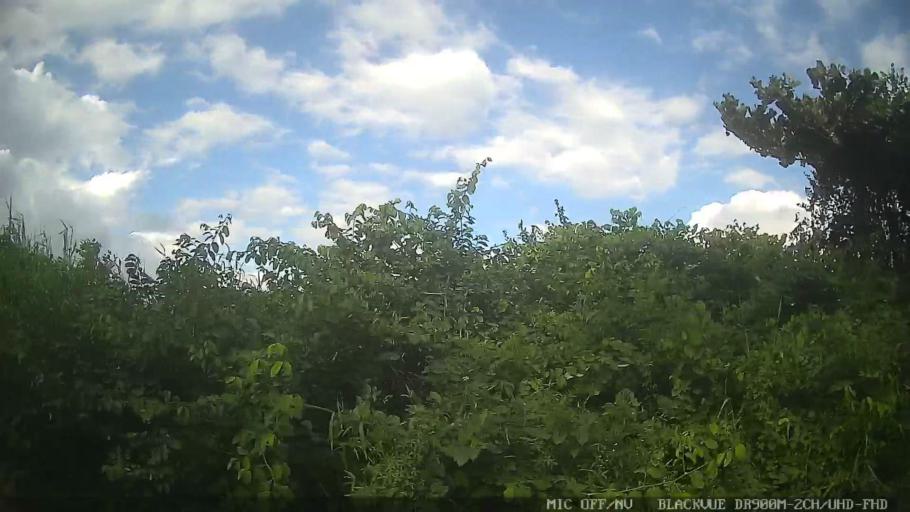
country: BR
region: Sao Paulo
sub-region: Sao Sebastiao
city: Sao Sebastiao
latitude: -23.7051
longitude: -45.4275
